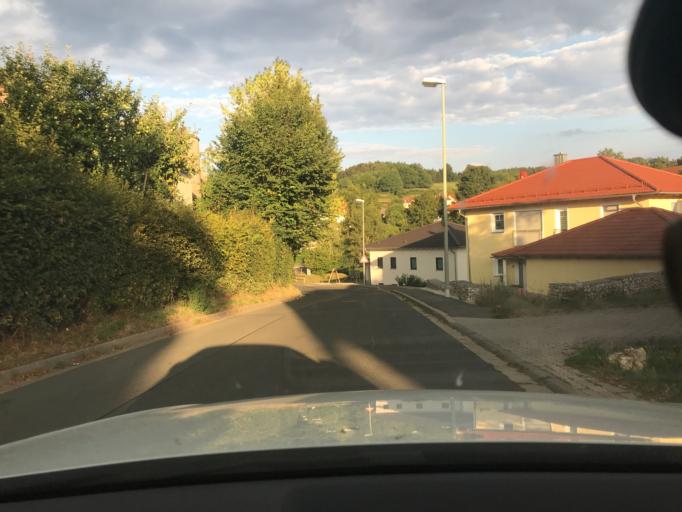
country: DE
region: Bavaria
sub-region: Upper Franconia
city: Pegnitz
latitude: 49.7453
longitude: 11.5603
